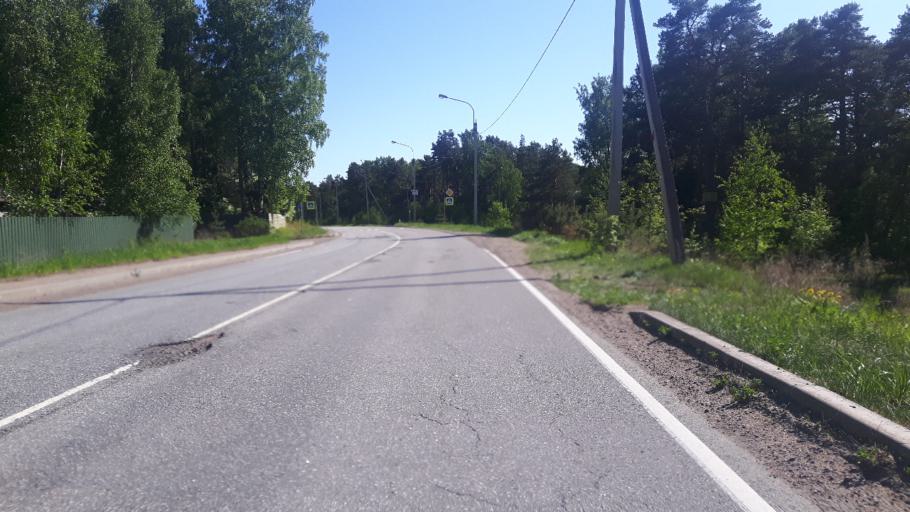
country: RU
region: Leningrad
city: Sosnovyy Bor
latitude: 60.1965
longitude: 29.0070
